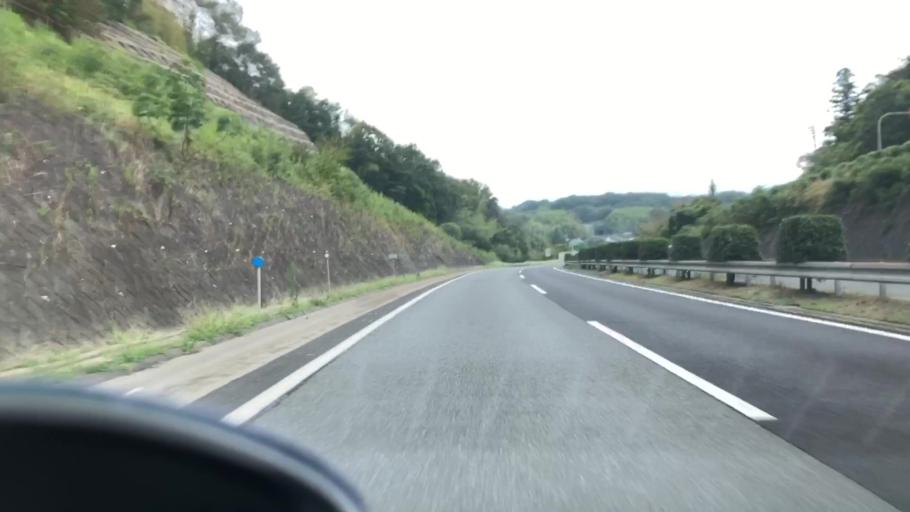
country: JP
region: Hyogo
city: Yashiro
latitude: 34.8911
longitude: 135.0925
